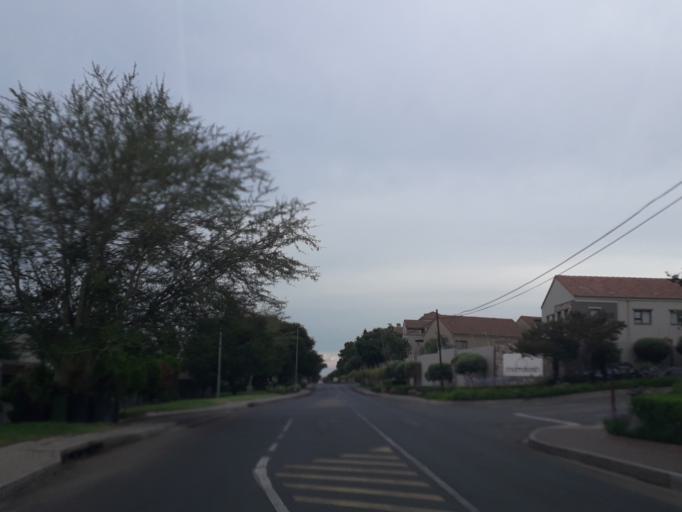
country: ZA
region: Gauteng
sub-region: City of Johannesburg Metropolitan Municipality
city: Diepsloot
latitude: -26.0439
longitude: 27.9895
